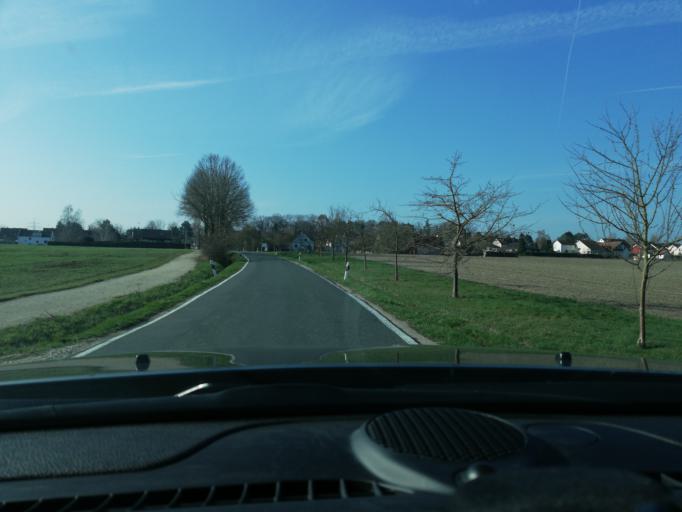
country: DE
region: Bavaria
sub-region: Regierungsbezirk Mittelfranken
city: Hessdorf
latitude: 49.6057
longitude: 10.9367
